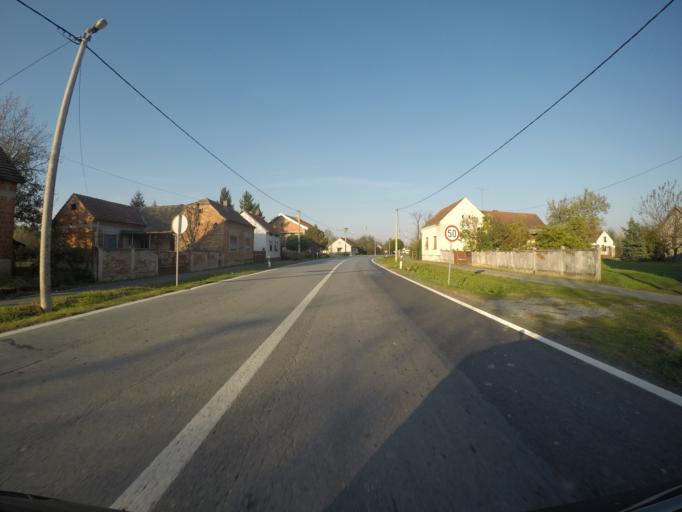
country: HU
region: Somogy
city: Barcs
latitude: 45.9033
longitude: 17.4404
